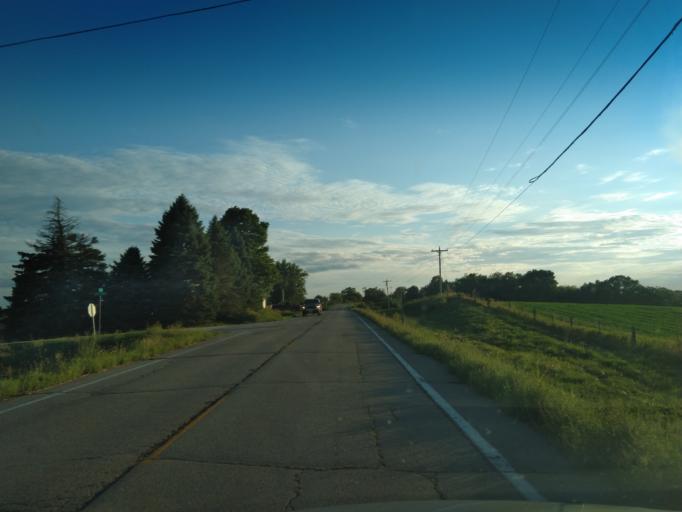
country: US
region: Iowa
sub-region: Jackson County
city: Maquoketa
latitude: 42.1484
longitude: -90.7587
